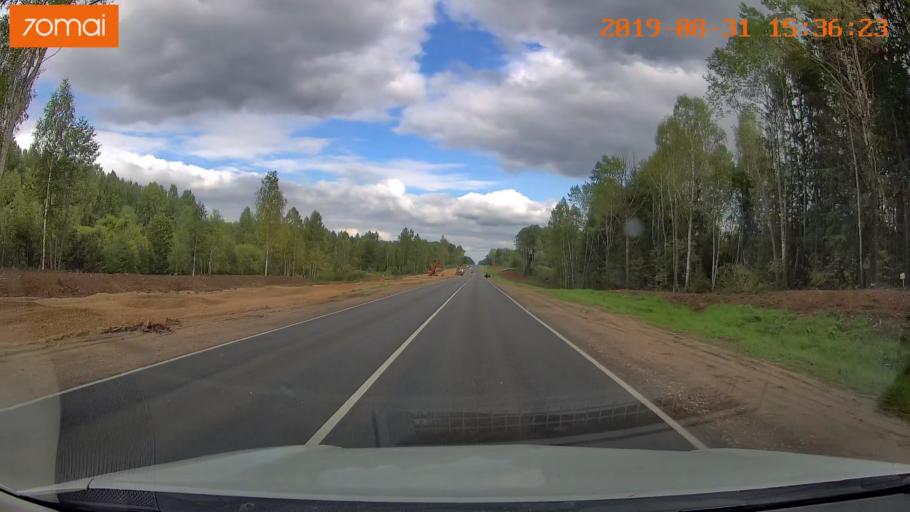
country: RU
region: Kaluga
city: Mosal'sk
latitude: 54.6109
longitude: 34.7579
